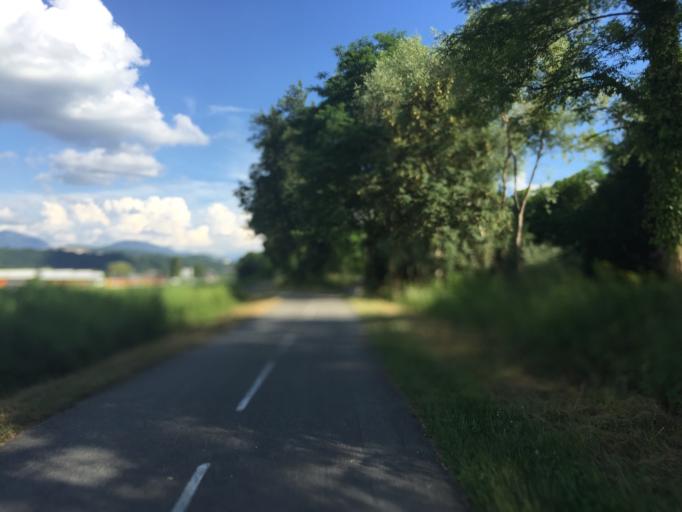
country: FR
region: Rhone-Alpes
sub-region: Departement de la Savoie
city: Le Bourget-du-Lac
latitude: 45.6235
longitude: 5.8753
